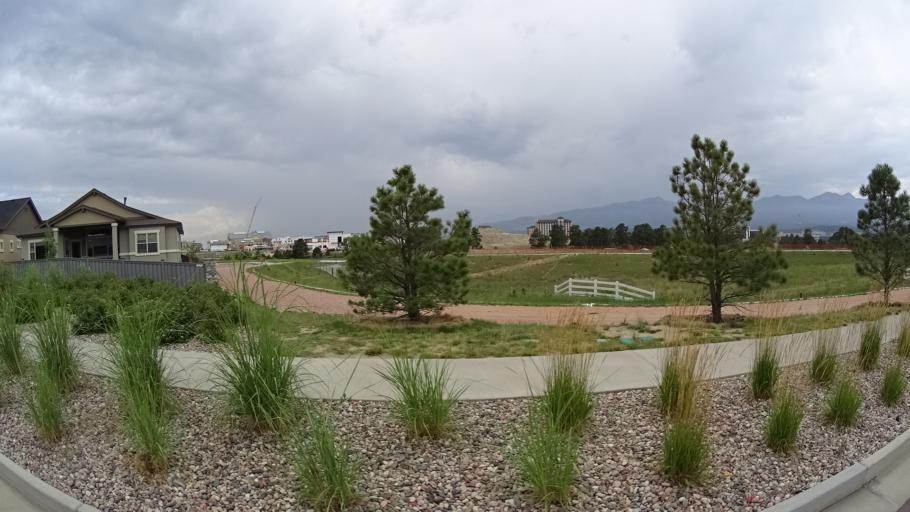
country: US
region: Colorado
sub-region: El Paso County
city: Gleneagle
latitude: 39.0002
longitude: -104.8048
